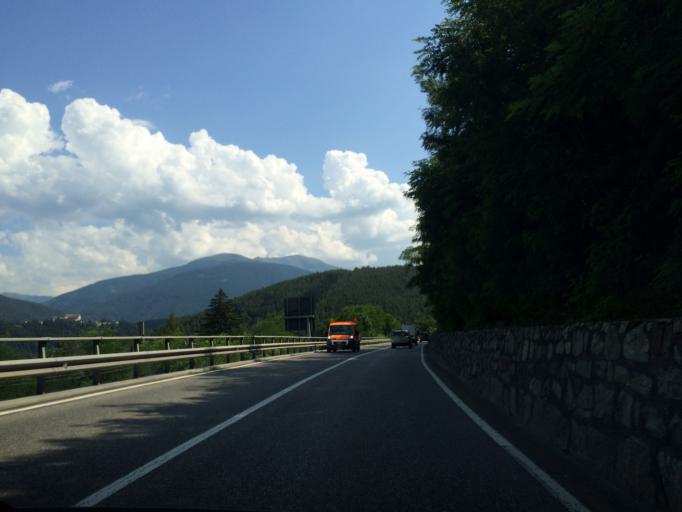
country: IT
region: Trentino-Alto Adige
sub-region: Bolzano
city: Rio di Pusteria
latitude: 46.7845
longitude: 11.6687
